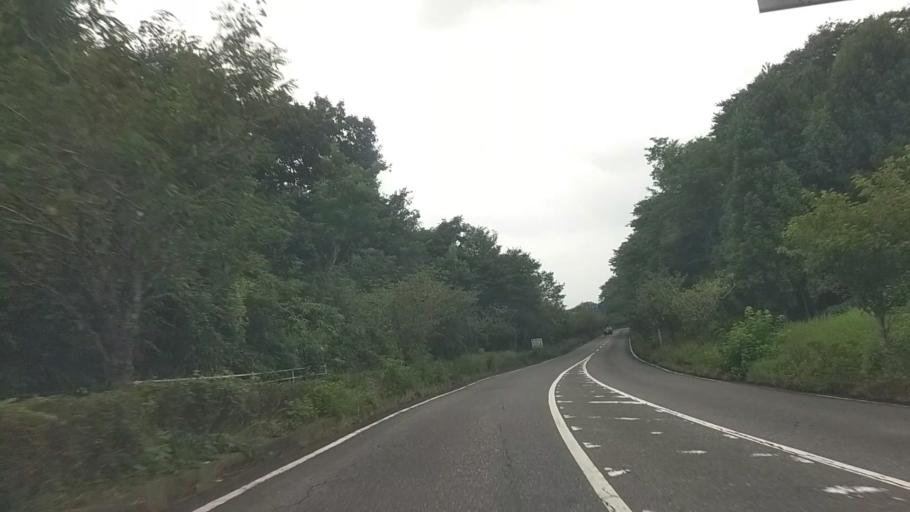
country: JP
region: Chiba
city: Kisarazu
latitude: 35.3845
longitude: 140.0057
